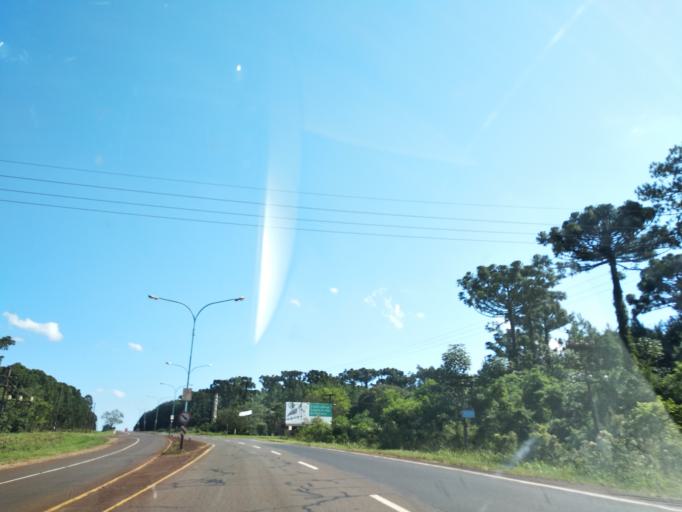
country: AR
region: Misiones
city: Puerto Piray
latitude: -26.4915
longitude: -54.6736
